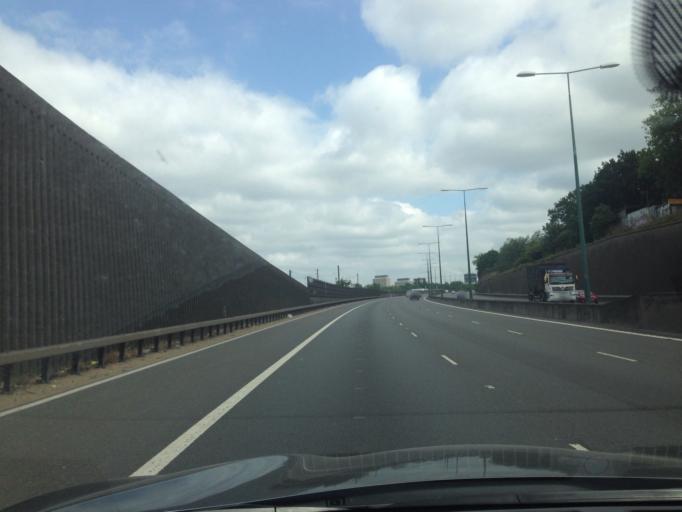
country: GB
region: England
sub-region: Greater London
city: Hendon
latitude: 51.5800
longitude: -0.2383
